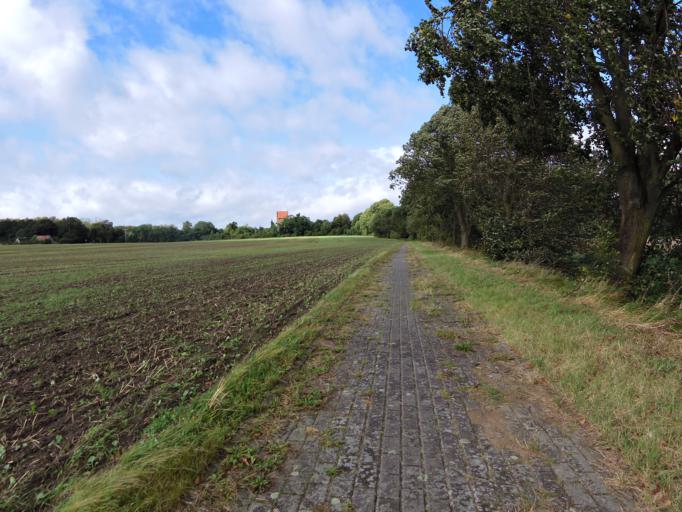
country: DE
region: Saxony-Anhalt
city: Hohenberg-Krusemark
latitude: 52.7504
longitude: 12.0118
